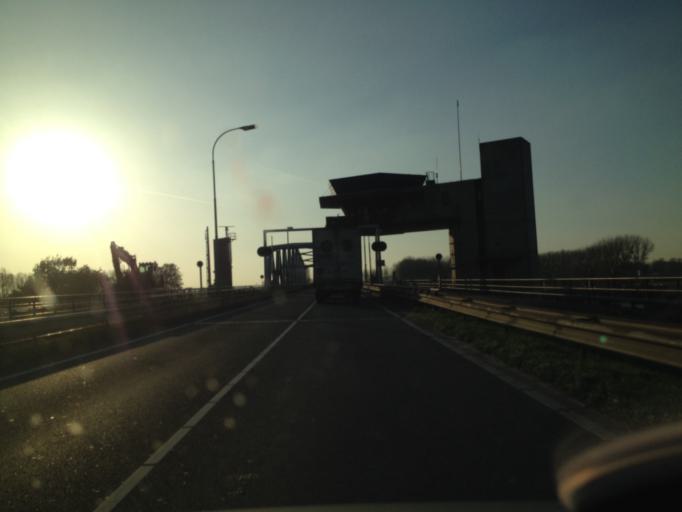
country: NL
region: Zeeland
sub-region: Gemeente Terneuzen
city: Sluiskil
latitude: 51.2941
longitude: 3.8376
